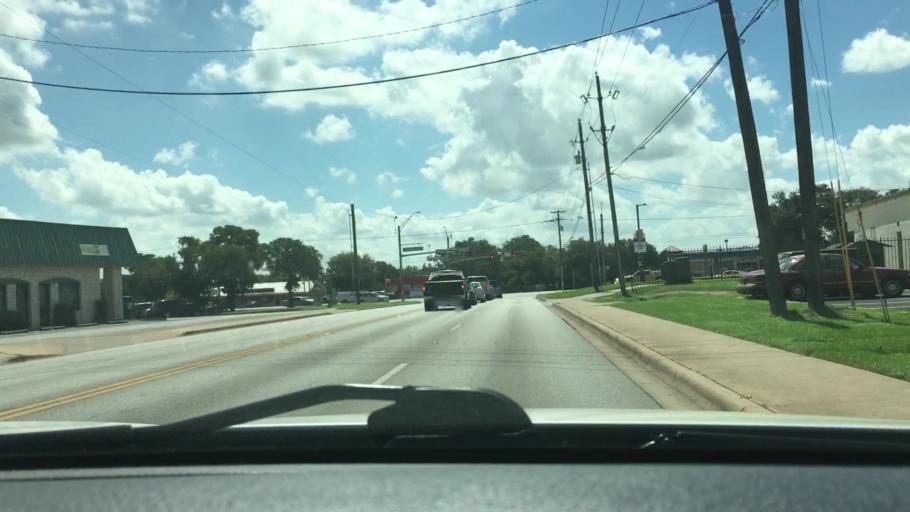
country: US
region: Texas
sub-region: Williamson County
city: Round Rock
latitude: 30.5191
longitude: -97.6679
